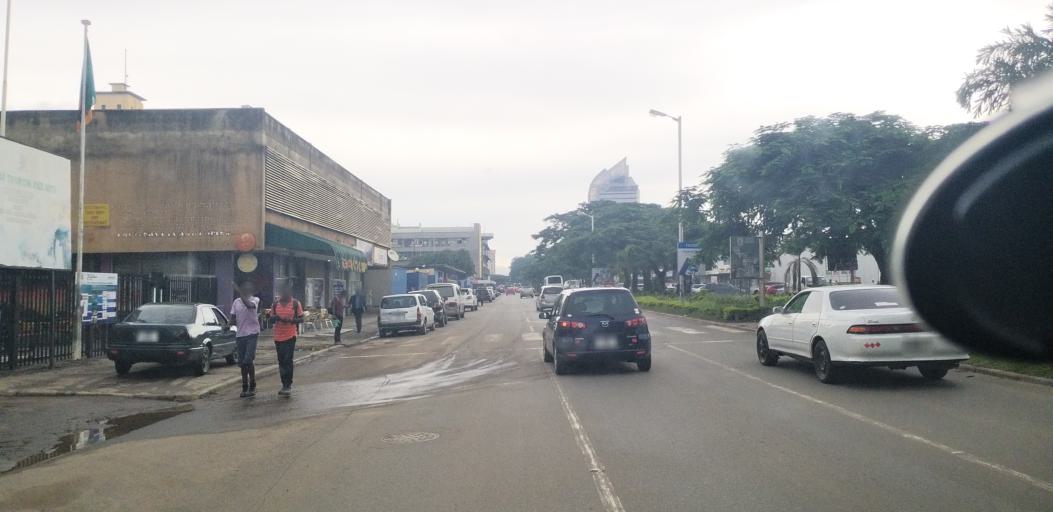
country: ZM
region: Lusaka
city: Lusaka
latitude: -15.4129
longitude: 28.2812
